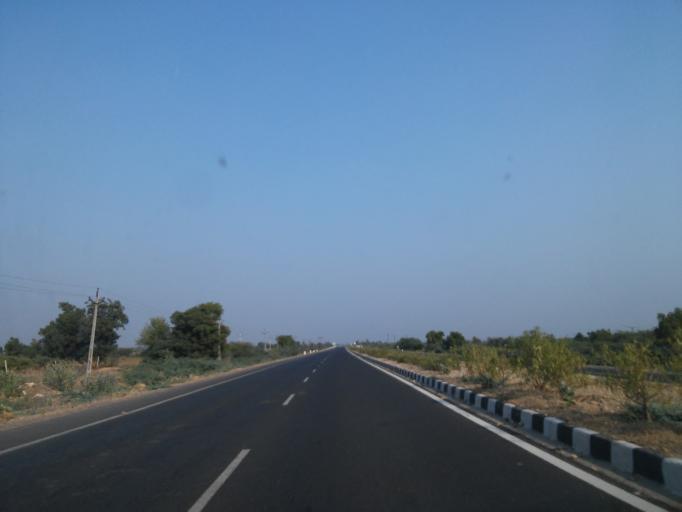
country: IN
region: Gujarat
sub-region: Surendranagar
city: Dhrangadhra
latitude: 23.0208
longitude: 71.5907
